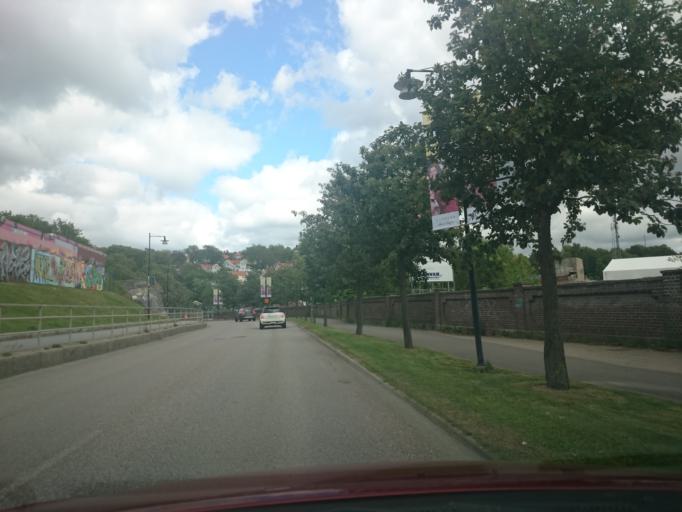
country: SE
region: Vaestra Goetaland
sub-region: Molndal
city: Moelndal
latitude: 57.6563
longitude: 12.0248
